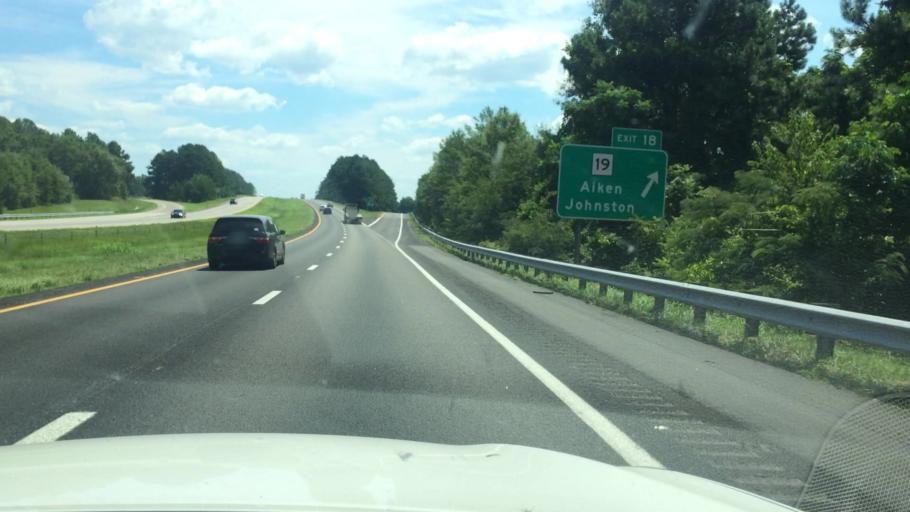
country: US
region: South Carolina
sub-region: Aiken County
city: Aiken
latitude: 33.6371
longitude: -81.7467
